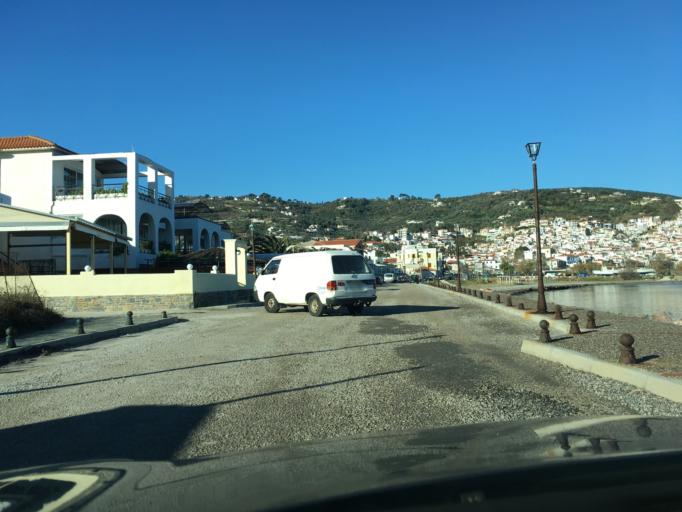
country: GR
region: Thessaly
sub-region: Nomos Magnisias
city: Skopelos
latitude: 39.1187
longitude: 23.7335
